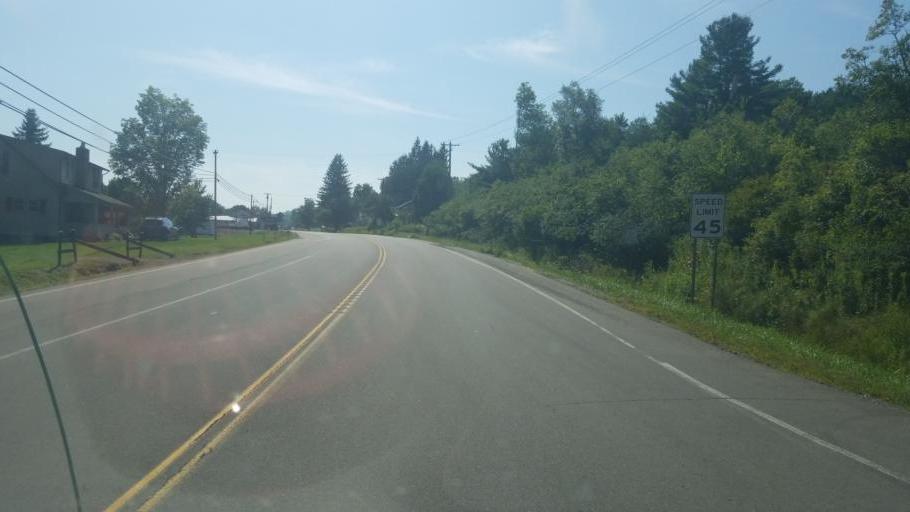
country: US
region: New York
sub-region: Allegany County
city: Wellsville
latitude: 42.1031
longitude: -78.0372
